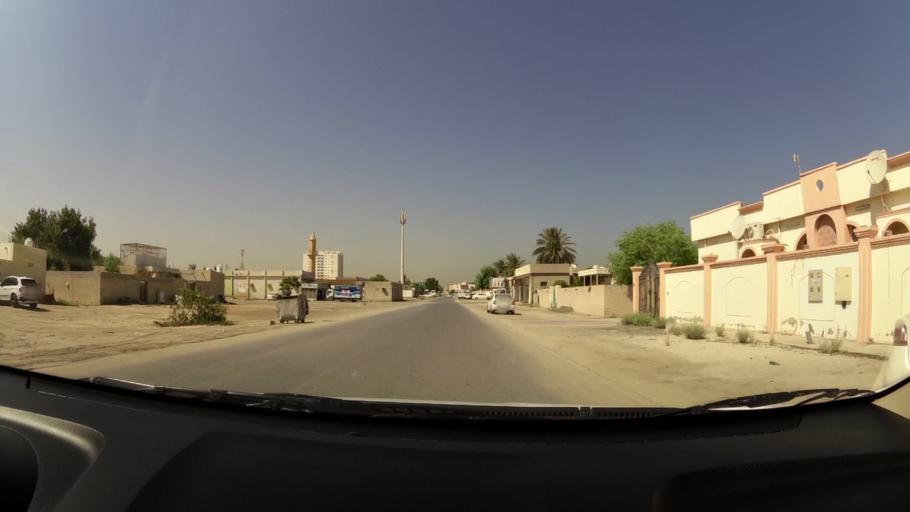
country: AE
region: Umm al Qaywayn
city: Umm al Qaywayn
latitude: 25.5843
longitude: 55.5628
